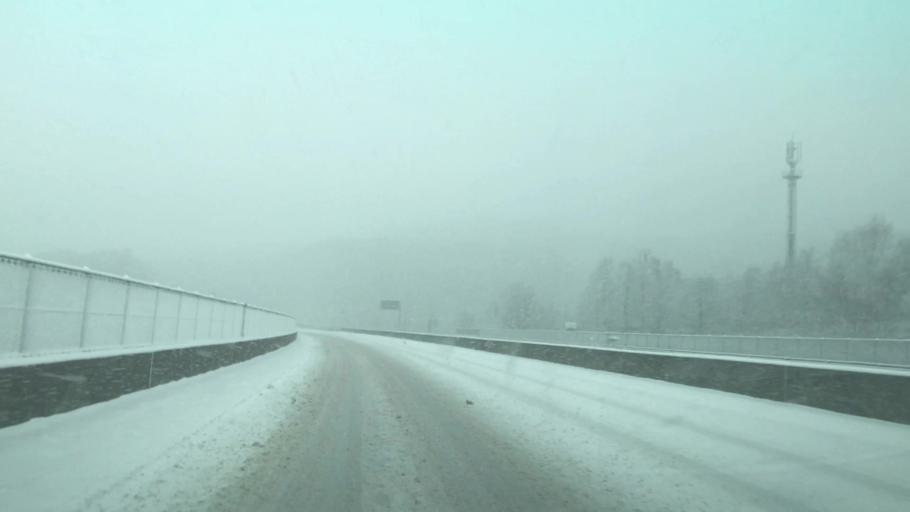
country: JP
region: Hokkaido
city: Muroran
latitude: 42.4168
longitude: 141.0805
